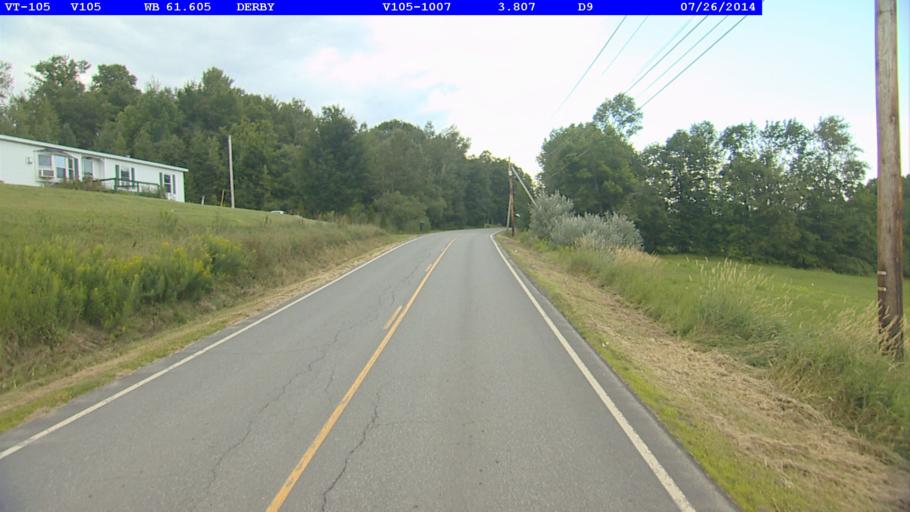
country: US
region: Vermont
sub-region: Orleans County
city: Newport
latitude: 44.9108
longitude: -72.0952
